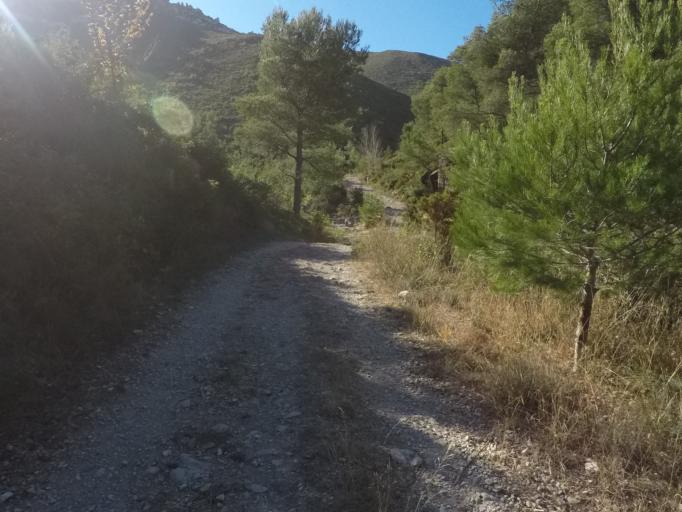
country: FR
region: Provence-Alpes-Cote d'Azur
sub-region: Departement des Bouches-du-Rhone
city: La Penne-sur-Huveaune
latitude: 43.2726
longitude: 5.4867
